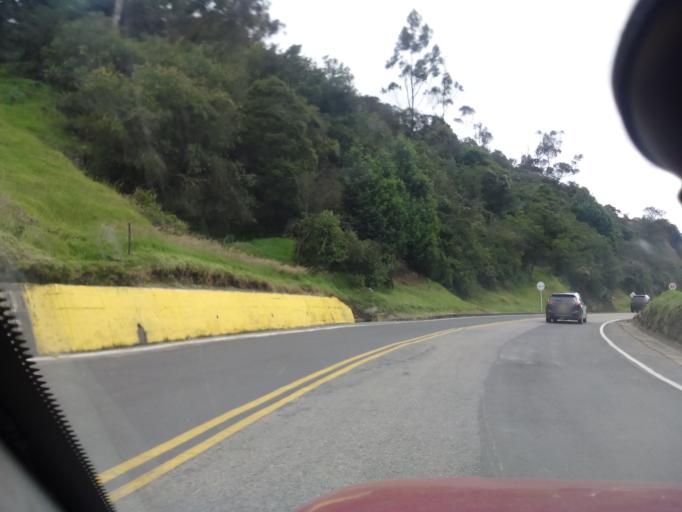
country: CO
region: Boyaca
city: Combita
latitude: 5.6648
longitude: -73.3632
